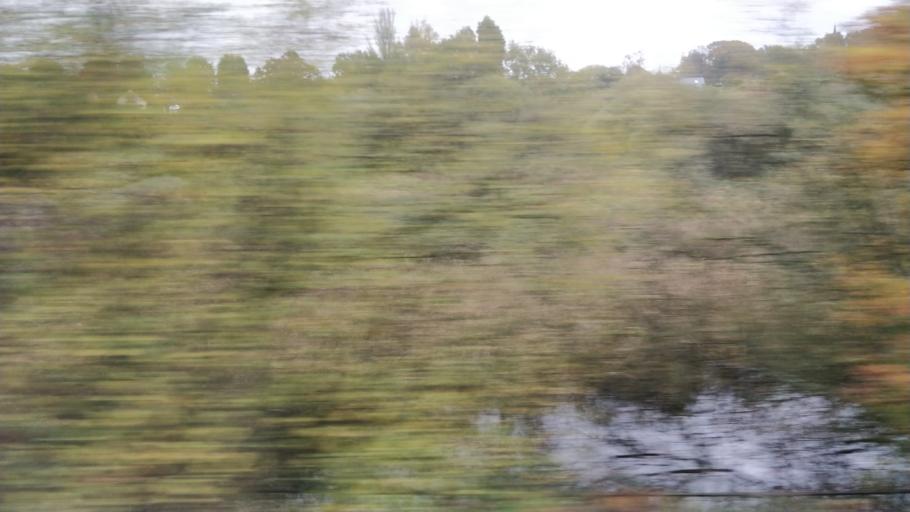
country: GB
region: England
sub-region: Lancashire
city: Parbold
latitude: 53.5879
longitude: -2.7590
